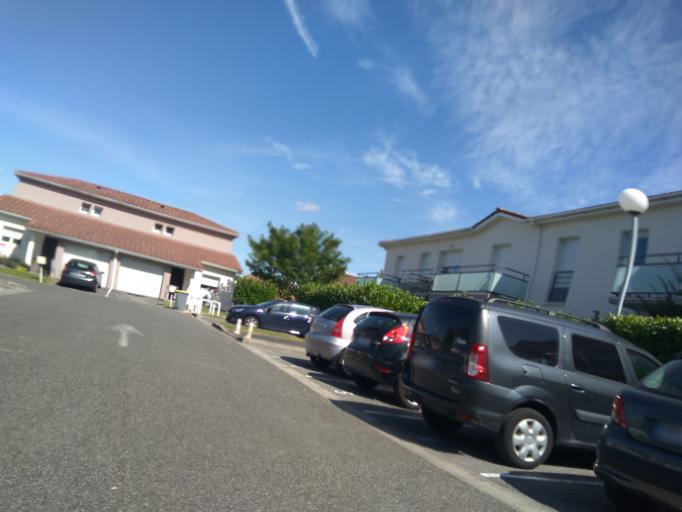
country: FR
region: Aquitaine
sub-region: Departement des Pyrenees-Atlantiques
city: Pau
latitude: 43.3125
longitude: -0.3396
